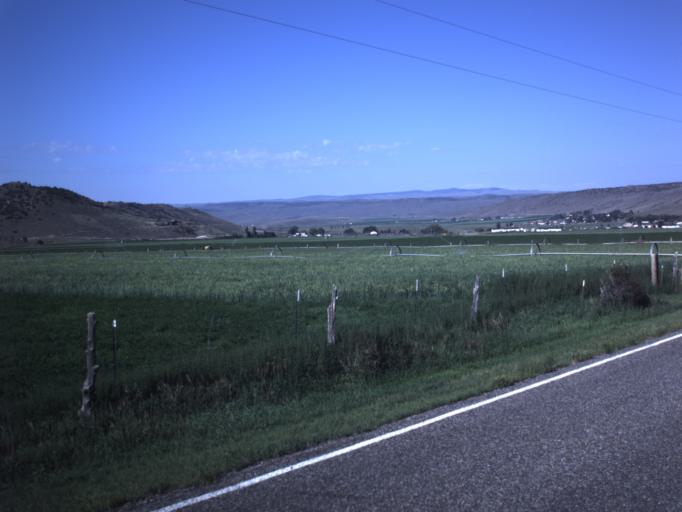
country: US
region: Utah
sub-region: Wayne County
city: Loa
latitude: 38.4695
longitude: -111.5820
